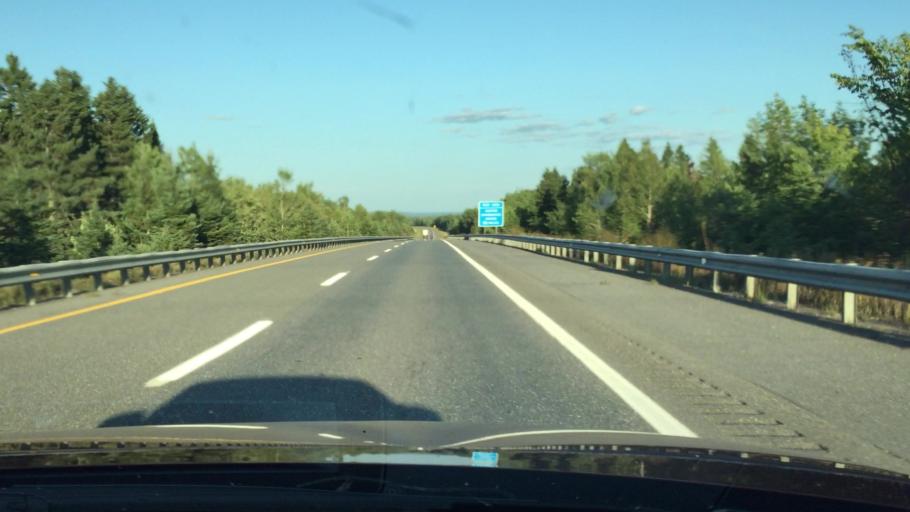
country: US
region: Maine
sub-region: Aroostook County
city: Hodgdon
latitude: 46.1428
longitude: -68.0400
